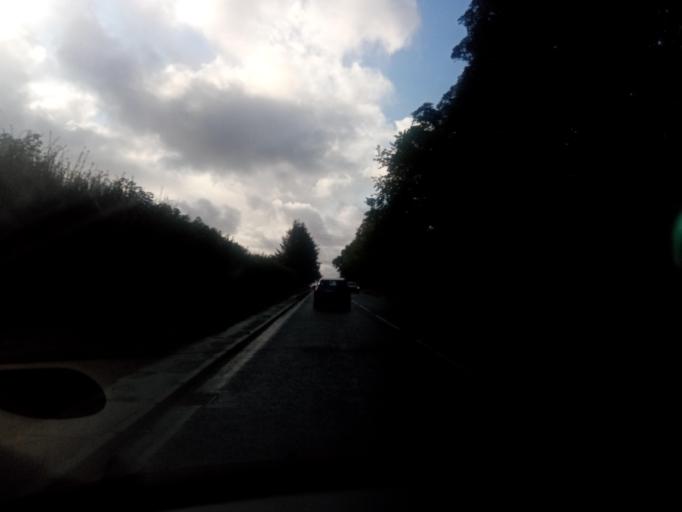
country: GB
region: England
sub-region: Cumbria
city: Carlisle
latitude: 54.9437
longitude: -2.9436
